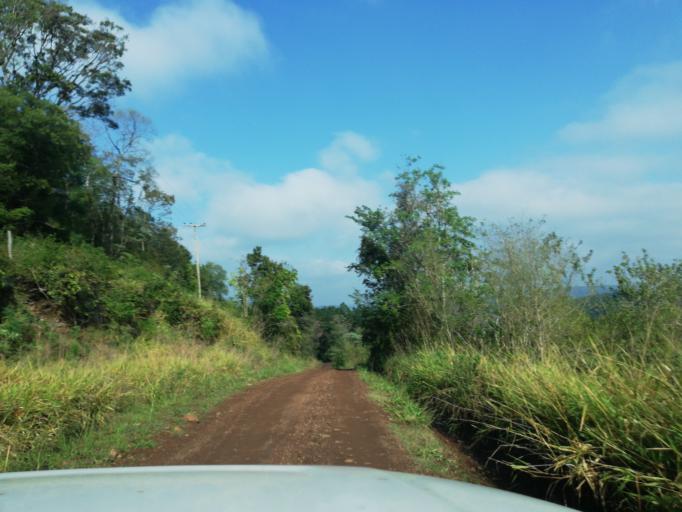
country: AR
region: Misiones
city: Cerro Azul
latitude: -27.5789
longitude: -55.5116
